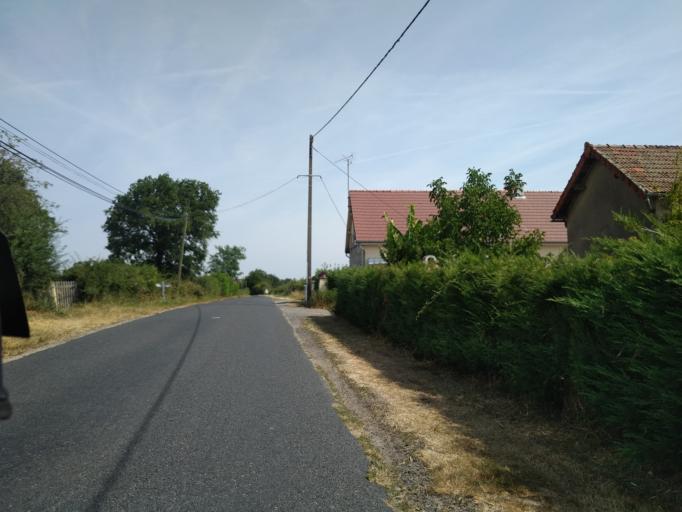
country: FR
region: Auvergne
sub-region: Departement de l'Allier
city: Molinet
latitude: 46.4184
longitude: 3.9763
